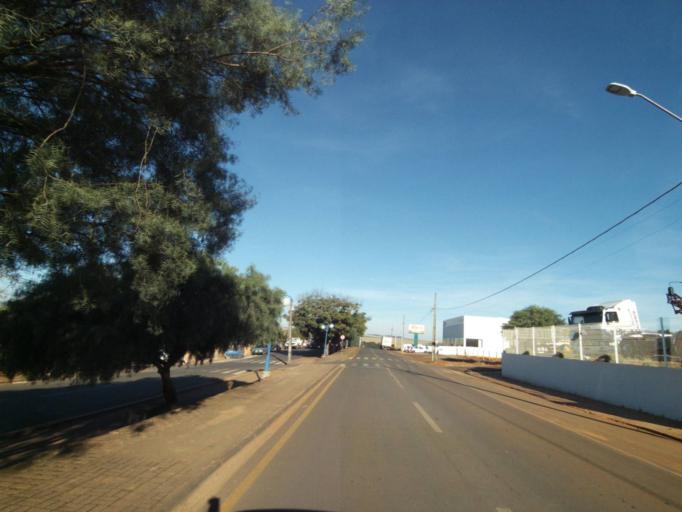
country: BR
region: Parana
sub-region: Tibagi
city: Tibagi
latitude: -24.5234
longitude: -50.4093
